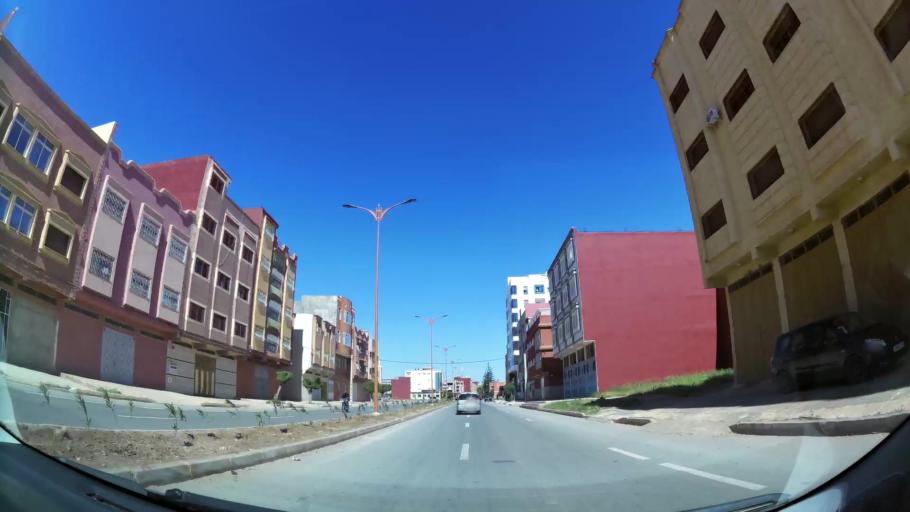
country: MA
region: Oriental
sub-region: Berkane-Taourirt
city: Berkane
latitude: 34.9343
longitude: -2.3289
